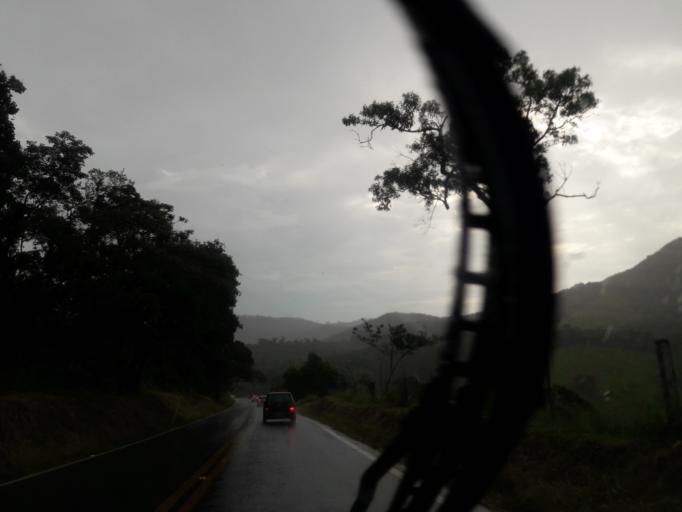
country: BR
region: Sao Paulo
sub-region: Aruja
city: Aruja
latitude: -23.3008
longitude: -46.4334
